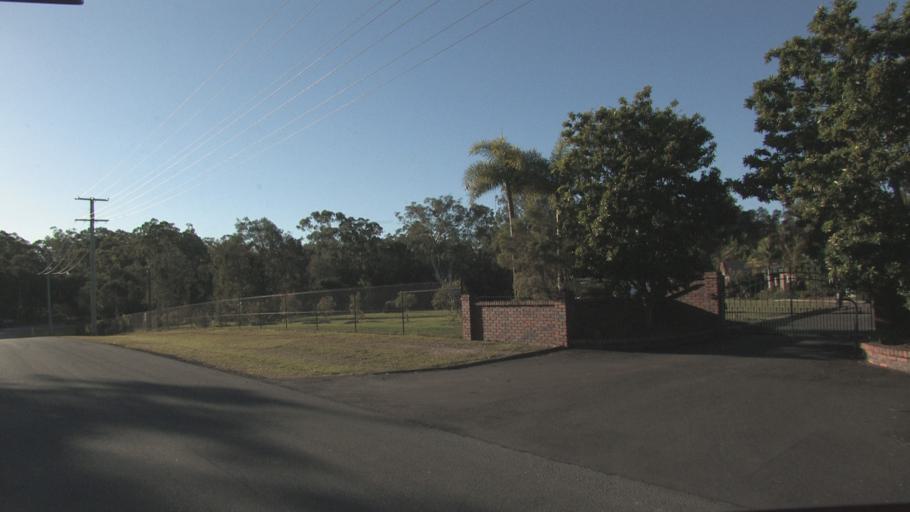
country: AU
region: Queensland
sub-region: Redland
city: Redland Bay
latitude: -27.6588
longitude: 153.2751
